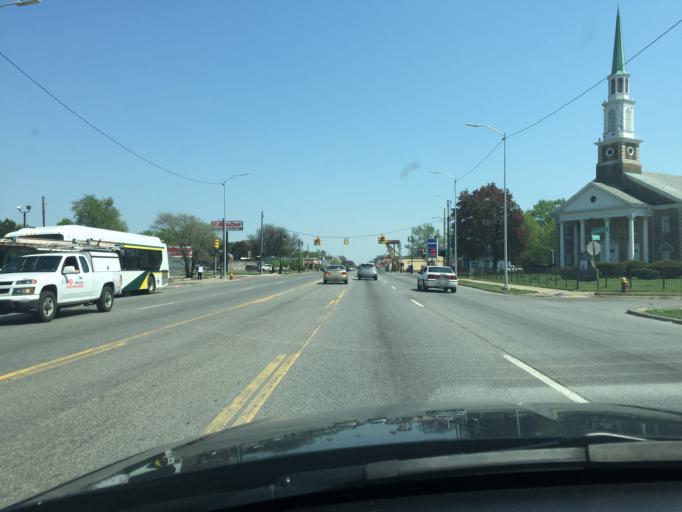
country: US
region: Michigan
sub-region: Wayne County
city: Redford
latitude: 42.4090
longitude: -83.2389
